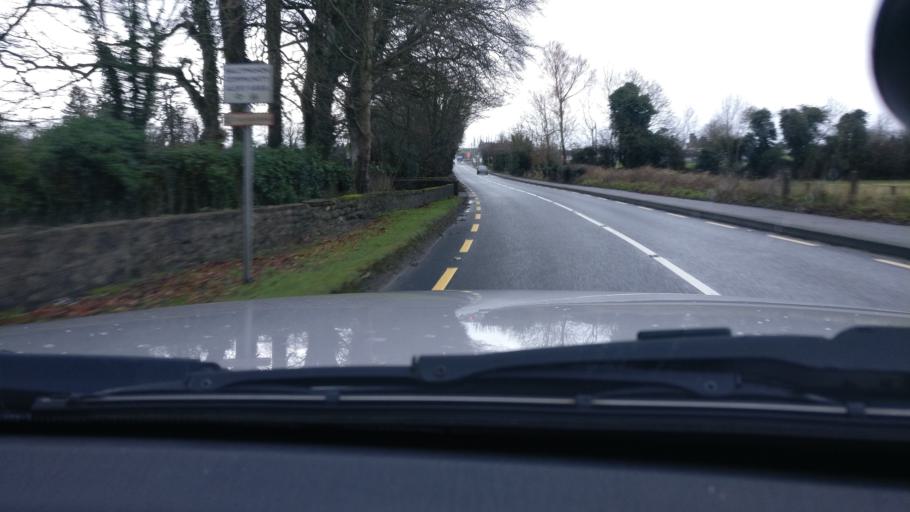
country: IE
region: Leinster
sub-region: An Longfort
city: Ballymahon
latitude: 53.5715
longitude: -7.7569
